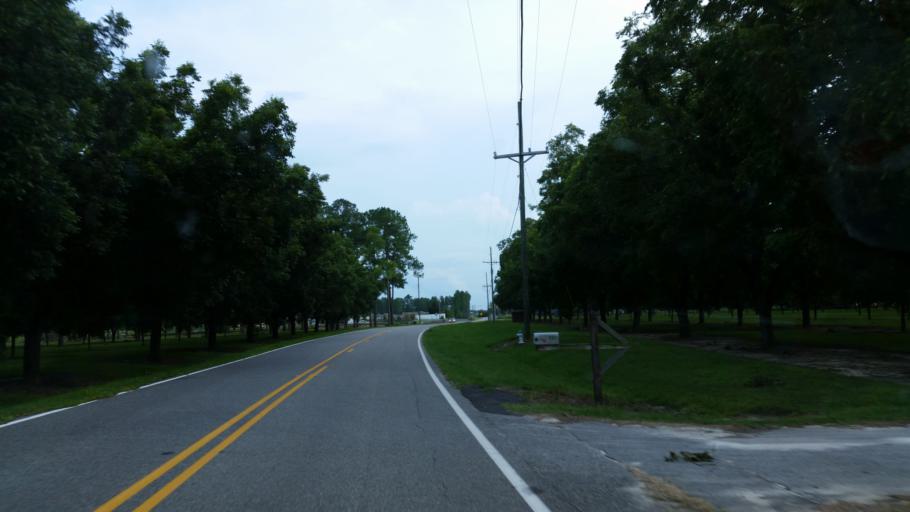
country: US
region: Georgia
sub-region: Lowndes County
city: Hahira
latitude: 31.0012
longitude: -83.3871
